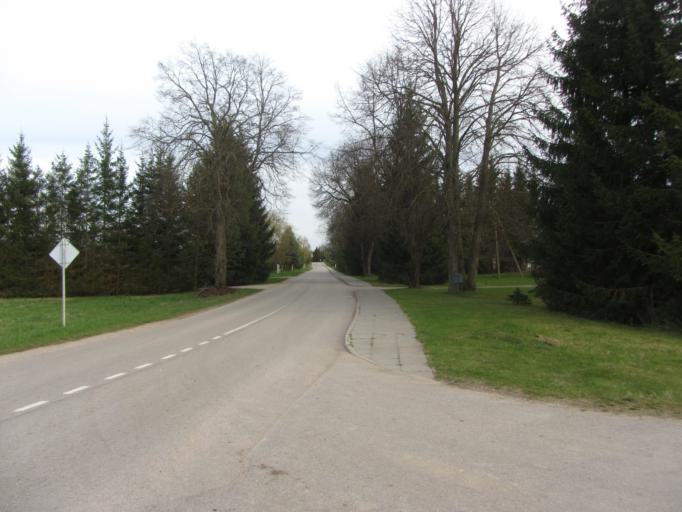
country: LT
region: Panevezys
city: Rokiskis
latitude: 55.7454
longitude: 25.8207
